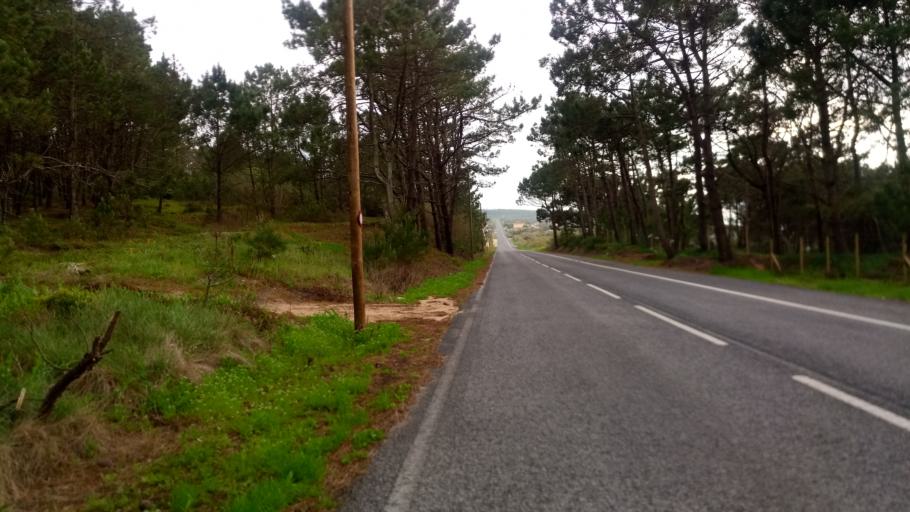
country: PT
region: Leiria
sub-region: Caldas da Rainha
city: Caldas da Rainha
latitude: 39.4865
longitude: -9.1782
